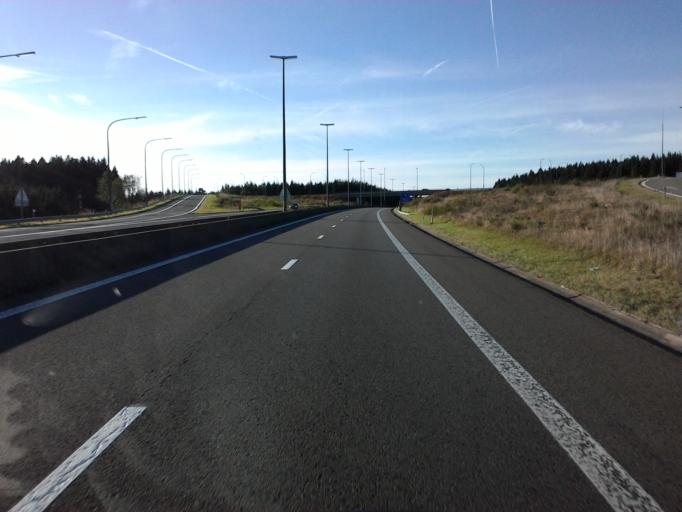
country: BE
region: Wallonia
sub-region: Province de Liege
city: Lierneux
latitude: 50.2468
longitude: 5.7349
